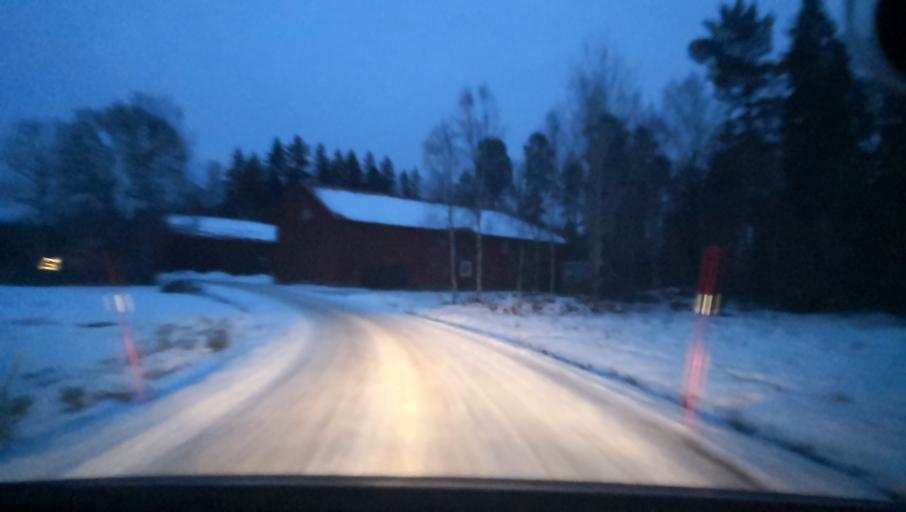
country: SE
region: Uppsala
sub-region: Heby Kommun
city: Tarnsjo
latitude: 60.2423
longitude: 16.6964
